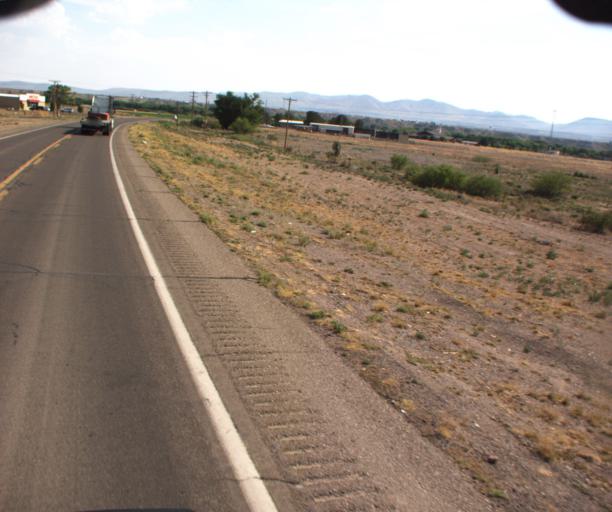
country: US
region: Arizona
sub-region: Greenlee County
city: Clifton
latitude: 32.7314
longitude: -109.0928
